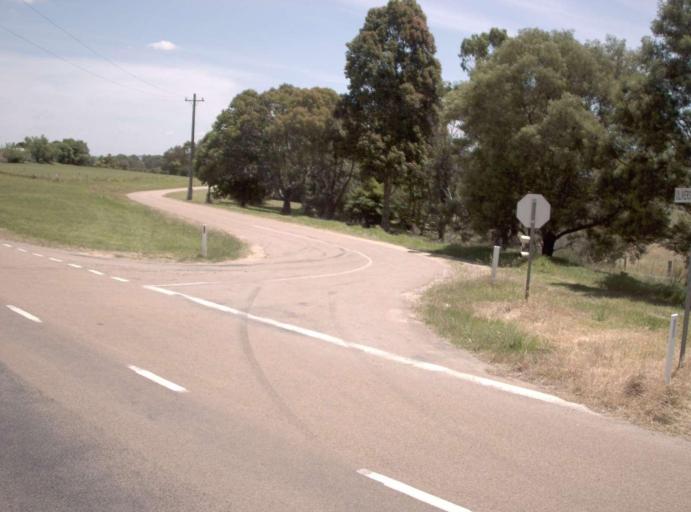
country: AU
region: Victoria
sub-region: East Gippsland
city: Bairnsdale
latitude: -37.7991
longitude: 147.6607
